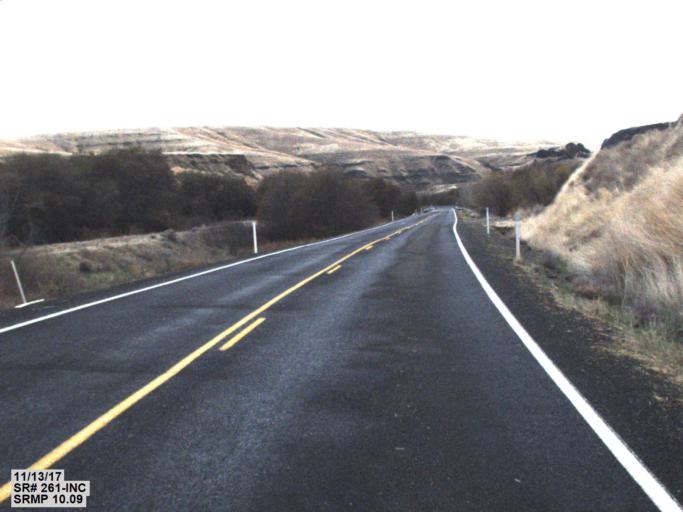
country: US
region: Washington
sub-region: Walla Walla County
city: Waitsburg
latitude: 46.5407
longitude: -118.1577
